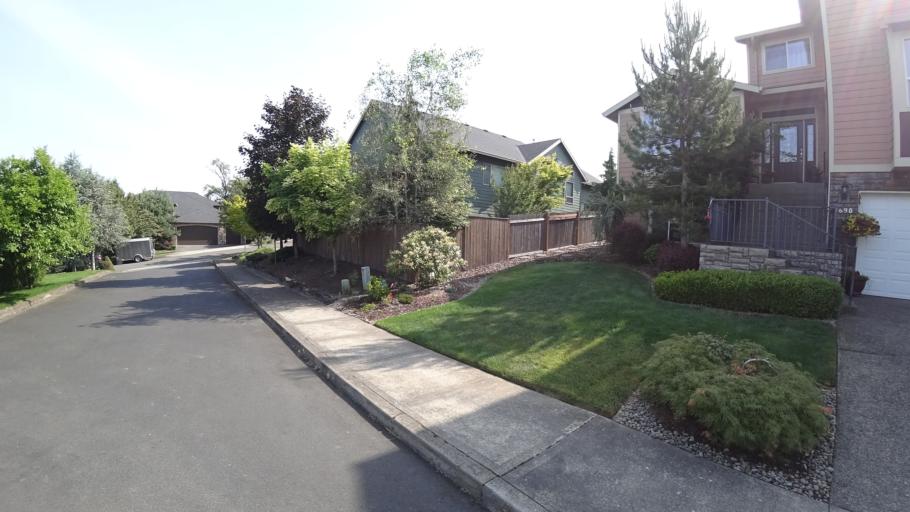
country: US
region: Oregon
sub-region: Clackamas County
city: Happy Valley
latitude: 45.4596
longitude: -122.5232
